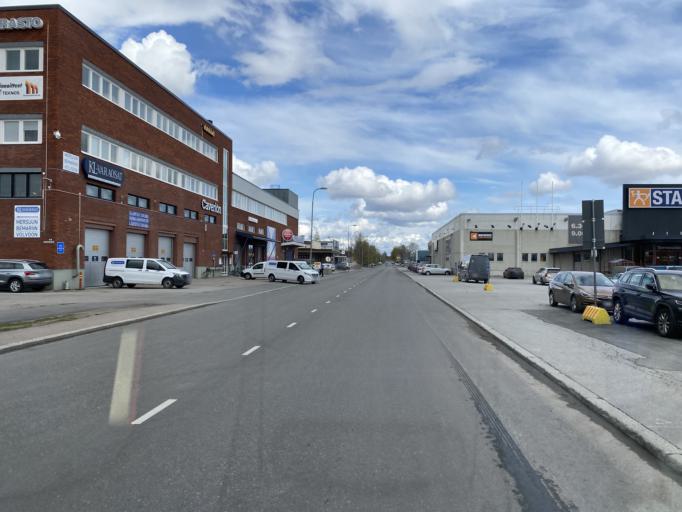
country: FI
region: Pirkanmaa
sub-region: Tampere
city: Tampere
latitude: 61.4796
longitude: 23.7832
